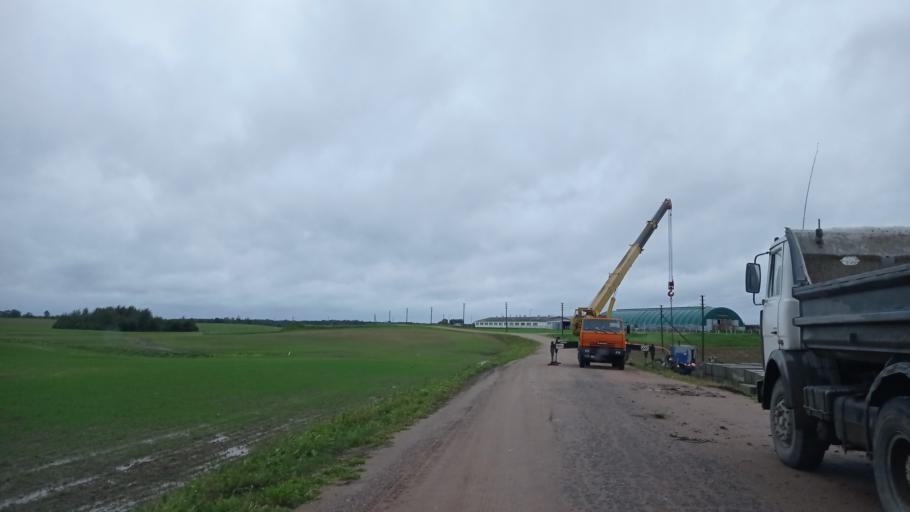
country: BY
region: Vitebsk
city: Haradok
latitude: 55.3408
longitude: 30.0969
